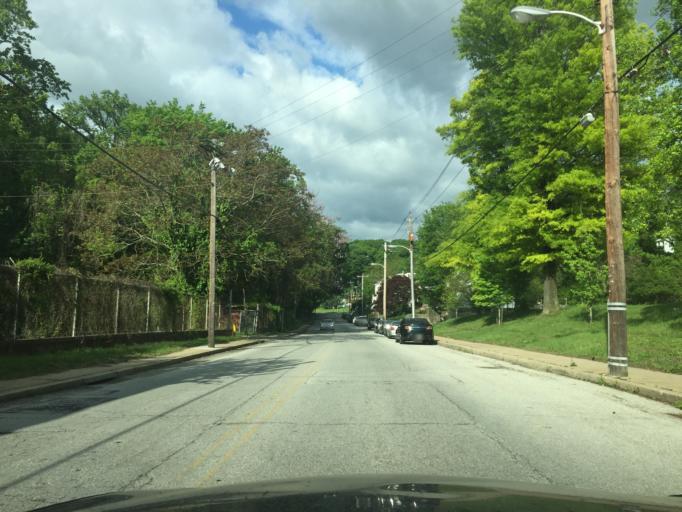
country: US
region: Maryland
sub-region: City of Baltimore
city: Baltimore
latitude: 39.3312
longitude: -76.6513
